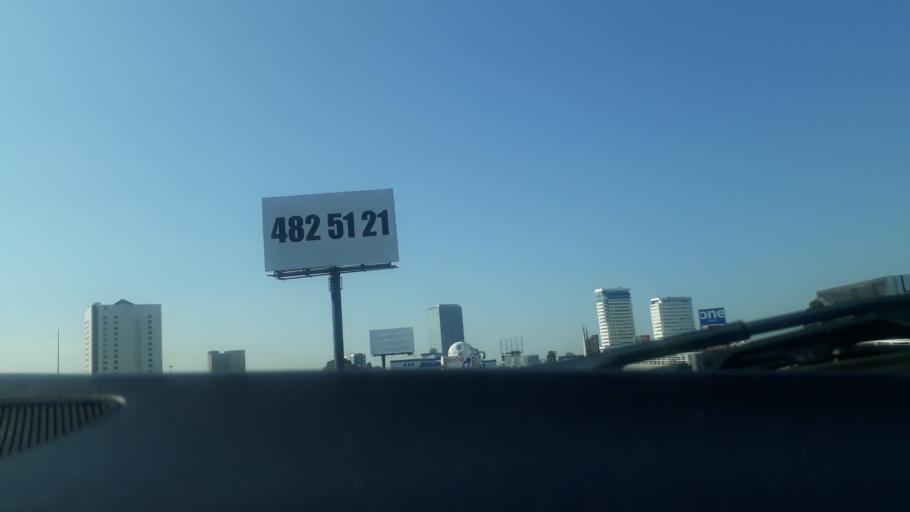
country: MX
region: Puebla
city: Tlazcalancingo
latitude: 19.0126
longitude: -98.2634
